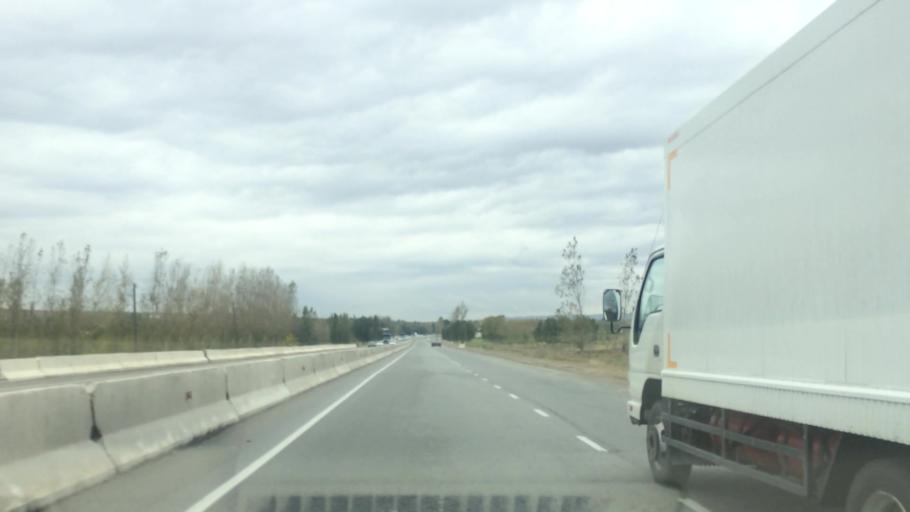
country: UZ
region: Jizzax
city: Jizzax
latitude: 39.9664
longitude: 67.5527
